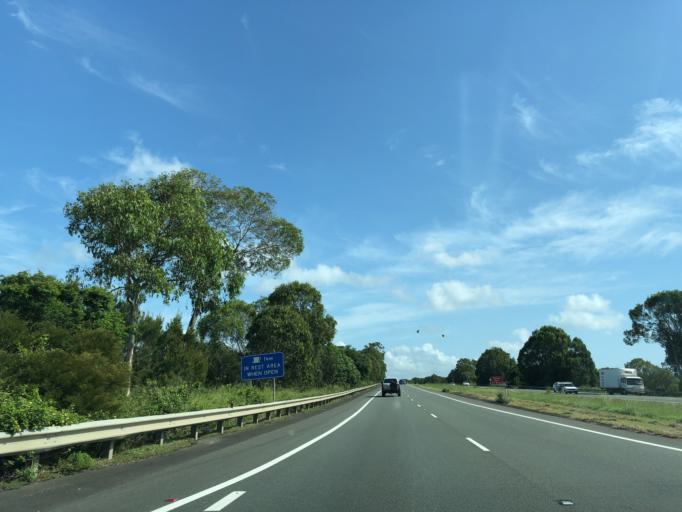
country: AU
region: New South Wales
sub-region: Byron Shire
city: Brunswick Heads
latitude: -28.6081
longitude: 153.5463
